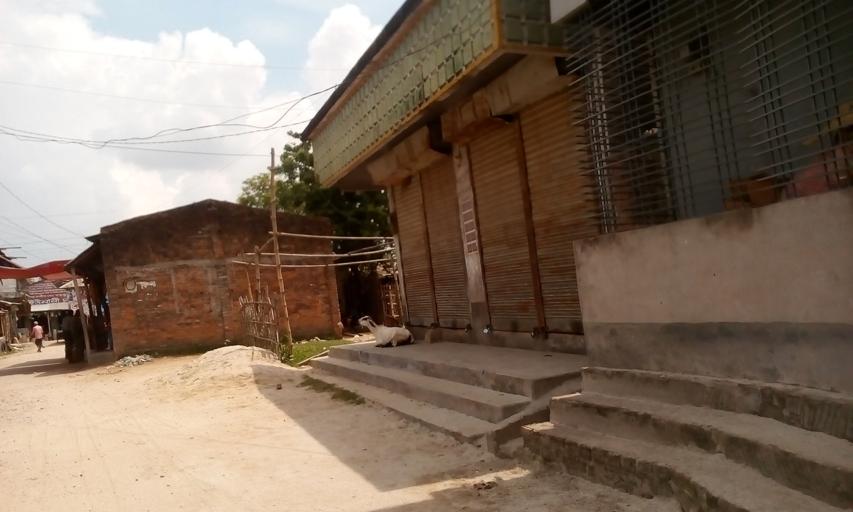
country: IN
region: West Bengal
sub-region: Dakshin Dinajpur
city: Balurghat
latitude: 25.3896
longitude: 88.9876
